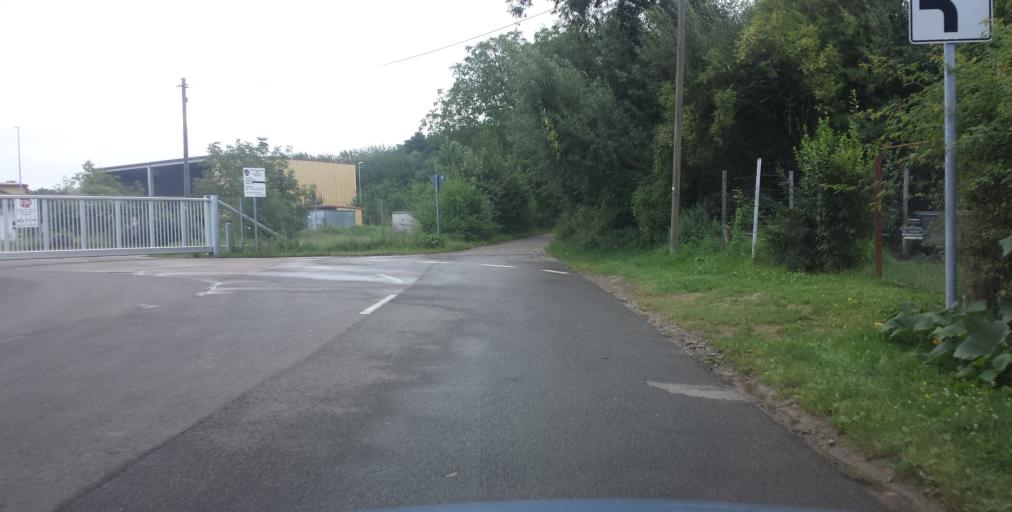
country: DE
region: Rheinland-Pfalz
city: Knoringen
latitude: 49.2489
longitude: 8.1395
